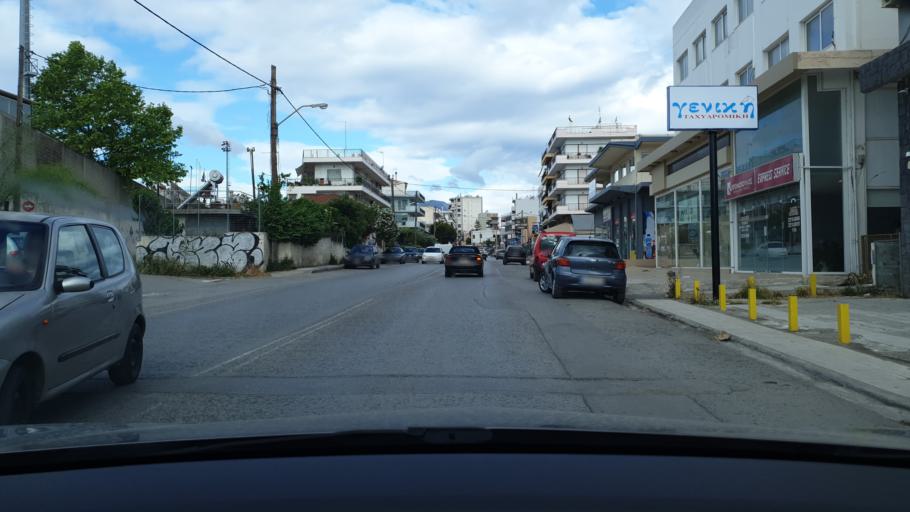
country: GR
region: Central Greece
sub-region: Nomos Evvoias
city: Chalkida
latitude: 38.4696
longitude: 23.6111
